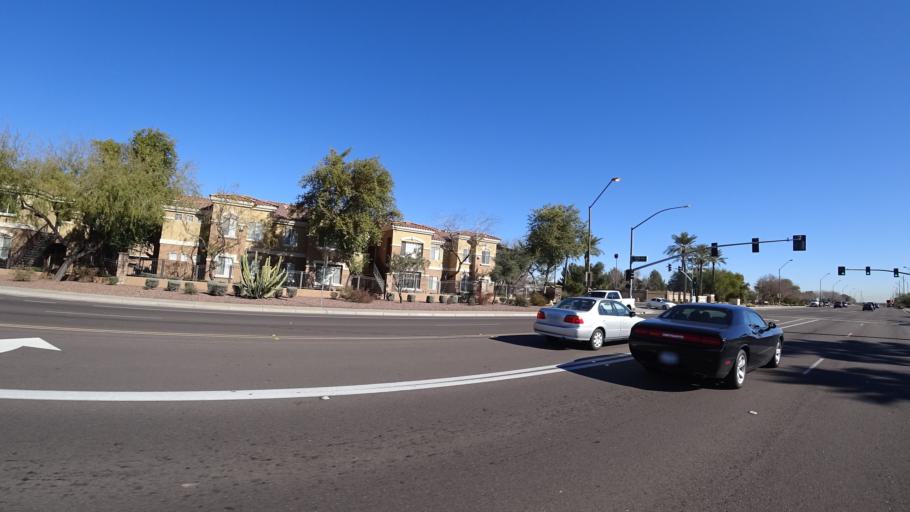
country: US
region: Arizona
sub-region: Maricopa County
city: Litchfield Park
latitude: 33.4932
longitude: -112.3330
